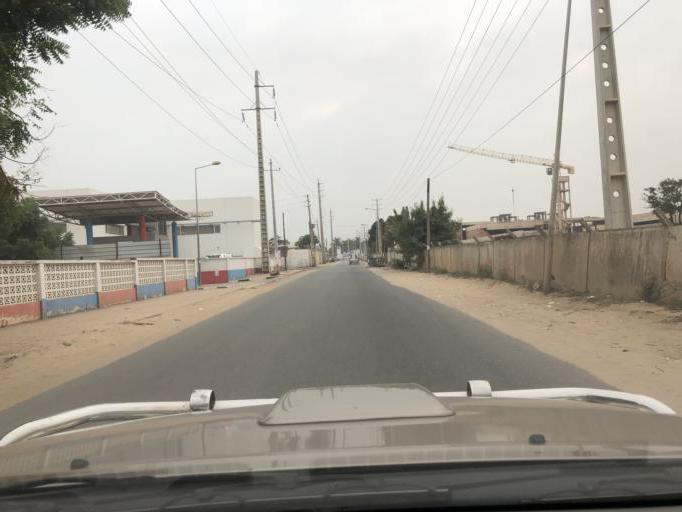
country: AO
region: Luanda
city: Luanda
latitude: -8.8902
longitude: 13.1892
